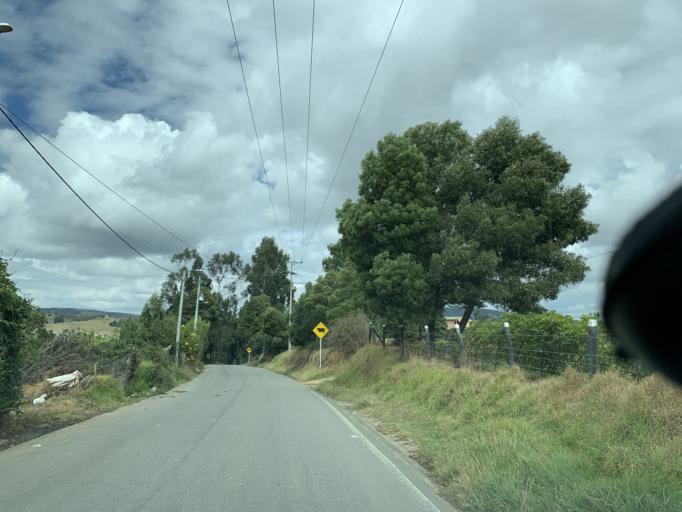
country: CO
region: Boyaca
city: Toca
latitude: 5.5676
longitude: -73.1938
